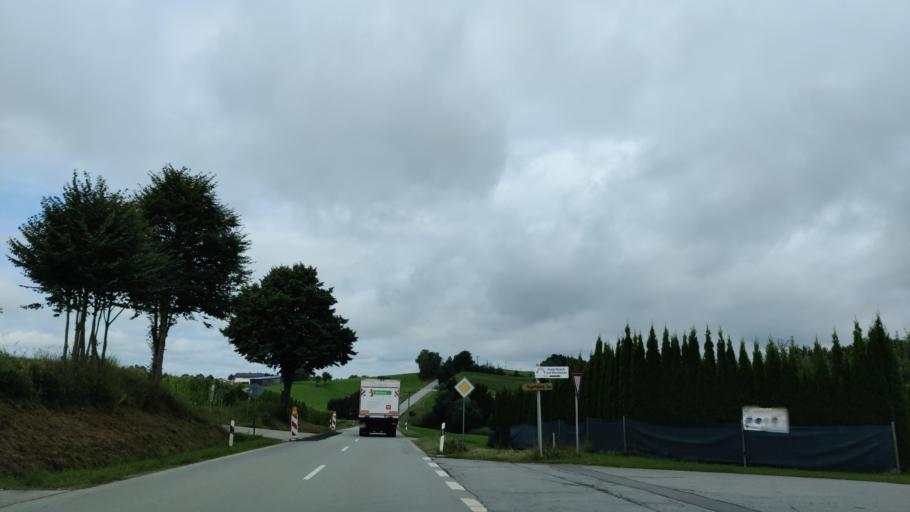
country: DE
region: Bavaria
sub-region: Lower Bavaria
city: Hofkirchen
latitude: 48.6753
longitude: 13.1617
